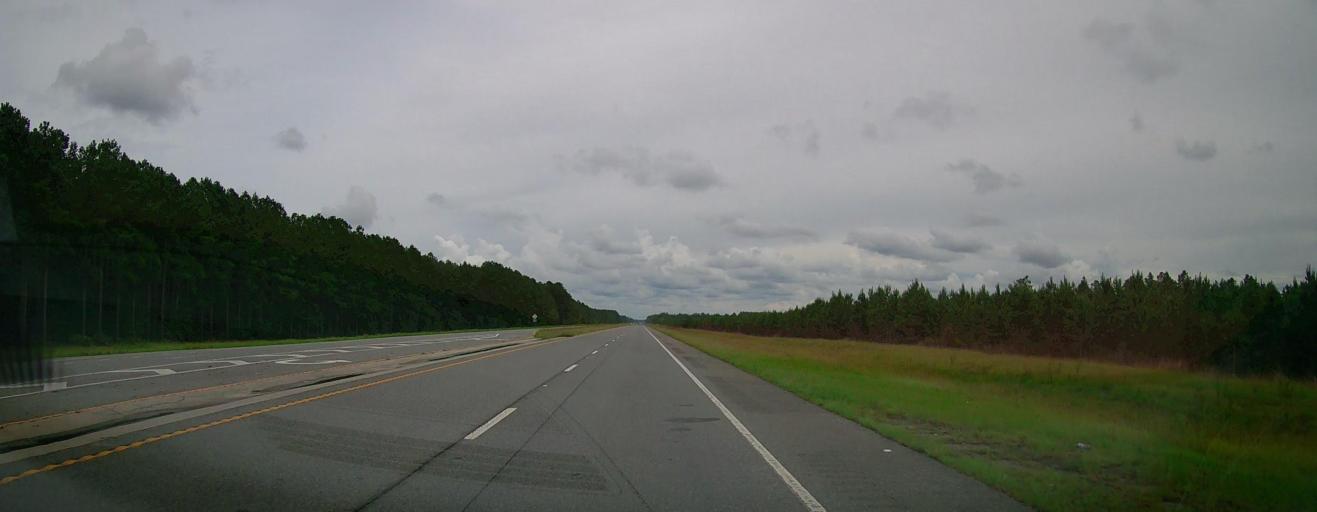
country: US
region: Georgia
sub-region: Appling County
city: Baxley
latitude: 31.7501
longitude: -82.2662
